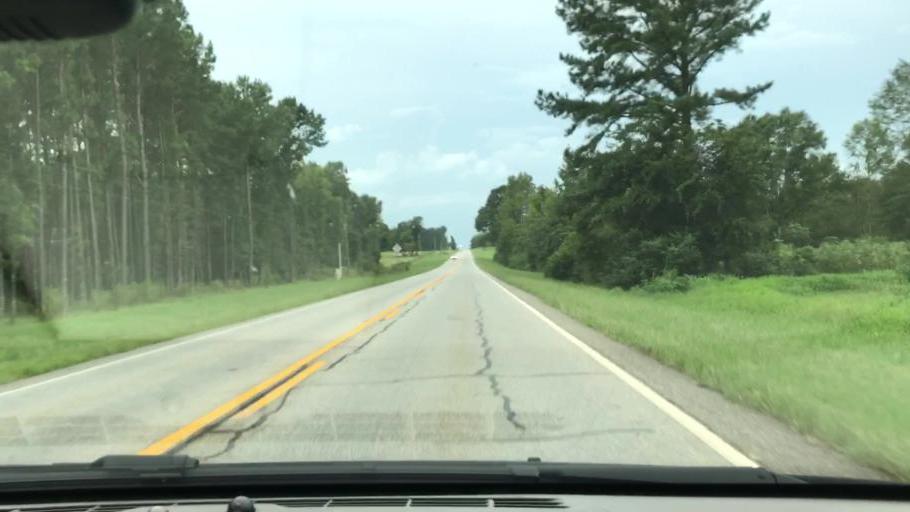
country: US
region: Georgia
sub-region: Early County
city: Blakely
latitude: 31.3298
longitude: -85.0020
